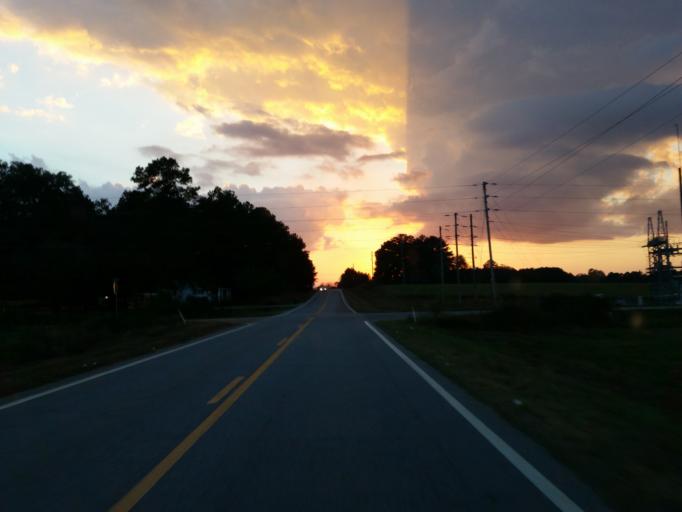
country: US
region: Georgia
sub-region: Dooly County
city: Unadilla
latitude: 32.1608
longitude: -83.6323
